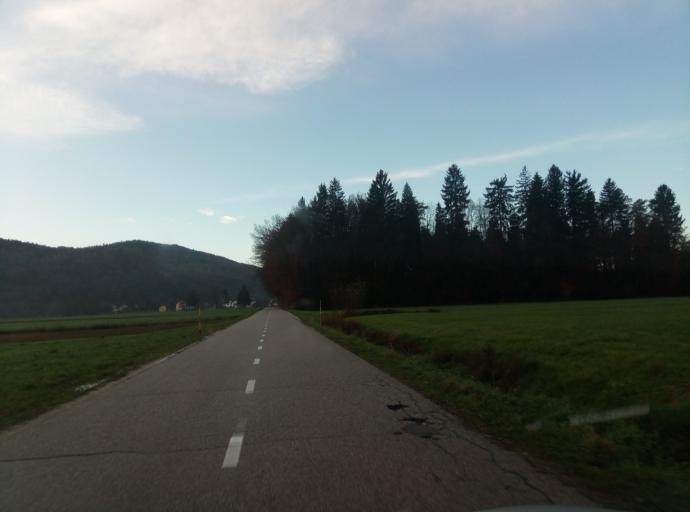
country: SI
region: Vodice
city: Vodice
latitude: 46.1669
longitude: 14.5188
